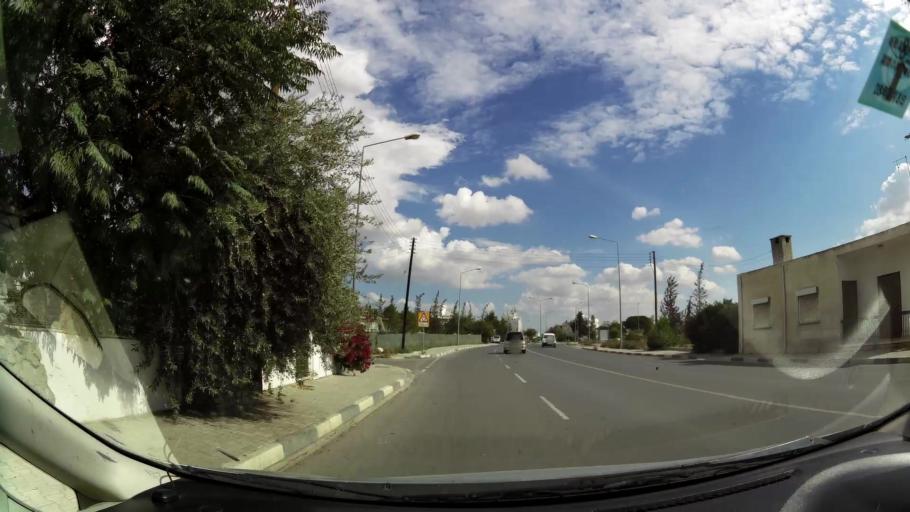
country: CY
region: Lefkosia
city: Nicosia
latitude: 35.1989
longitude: 33.3563
